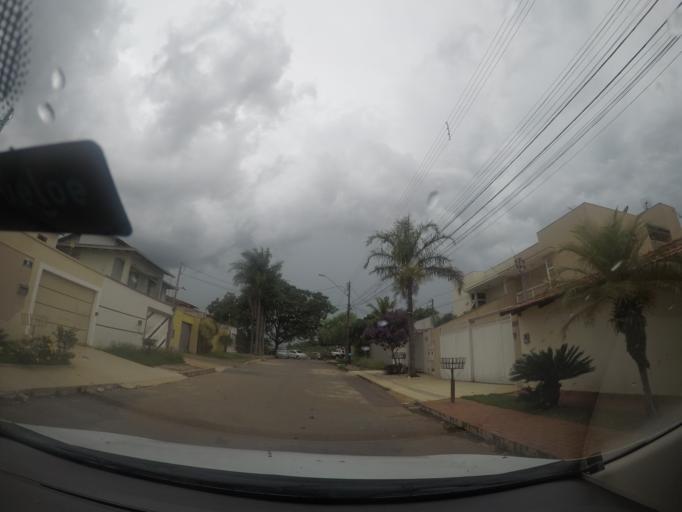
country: BR
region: Goias
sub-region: Goiania
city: Goiania
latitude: -16.6387
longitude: -49.2257
